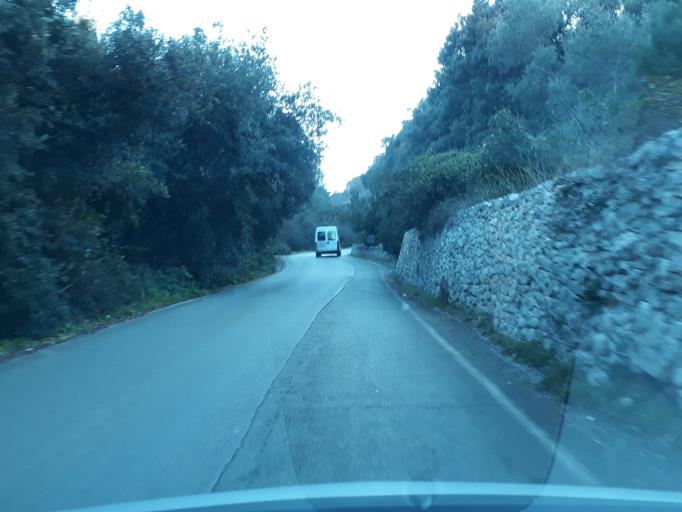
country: IT
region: Apulia
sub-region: Provincia di Brindisi
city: Lamie di Olimpie-Selva
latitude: 40.8051
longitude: 17.3523
